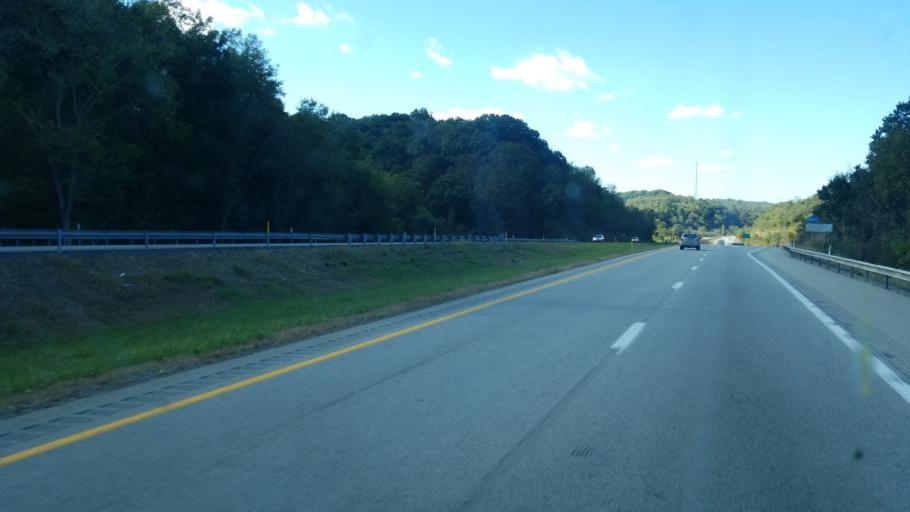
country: US
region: Pennsylvania
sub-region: Greene County
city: Waynesburg
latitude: 39.9522
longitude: -80.1660
